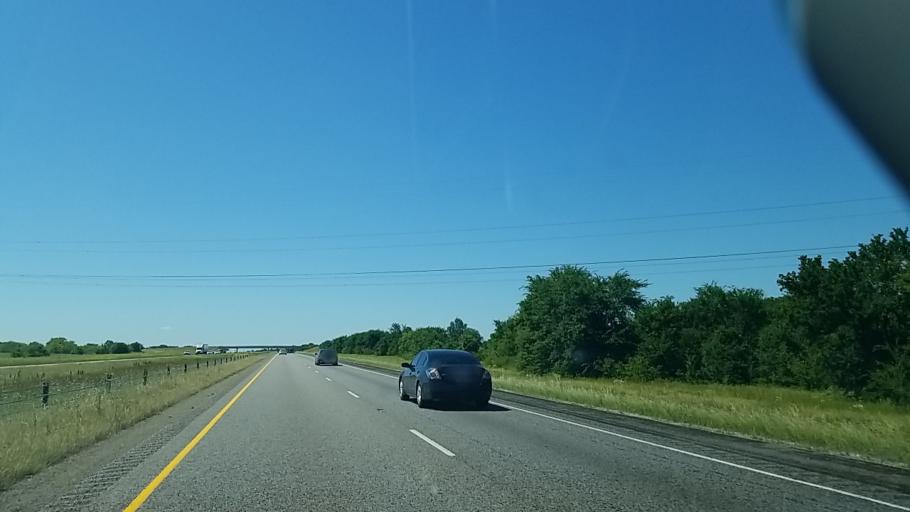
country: US
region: Texas
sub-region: Freestone County
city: Fairfield
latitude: 31.8239
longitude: -96.2799
